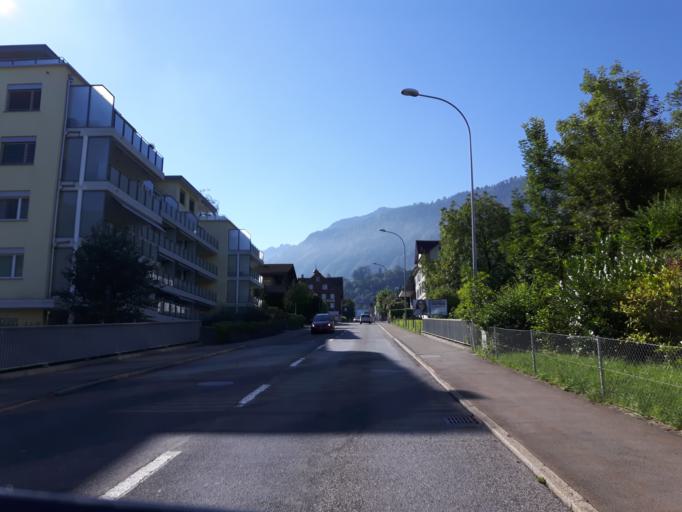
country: CH
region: Schwyz
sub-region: Bezirk Schwyz
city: Goldau
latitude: 47.0483
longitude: 8.5451
